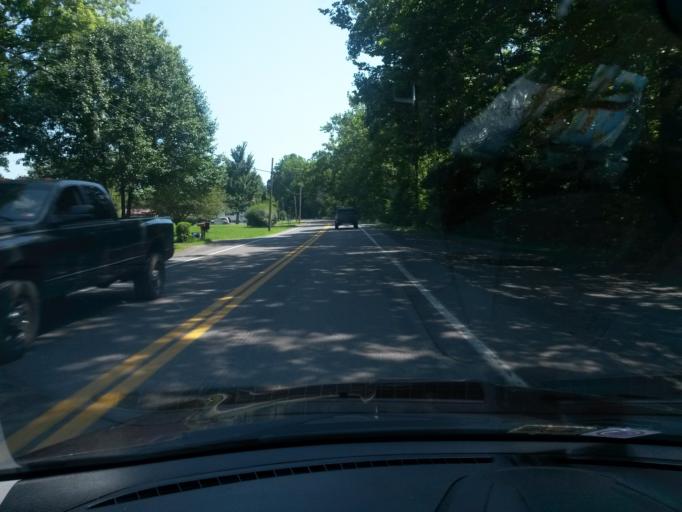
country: US
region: West Virginia
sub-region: Mineral County
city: Keyser
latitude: 39.3888
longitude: -79.0157
